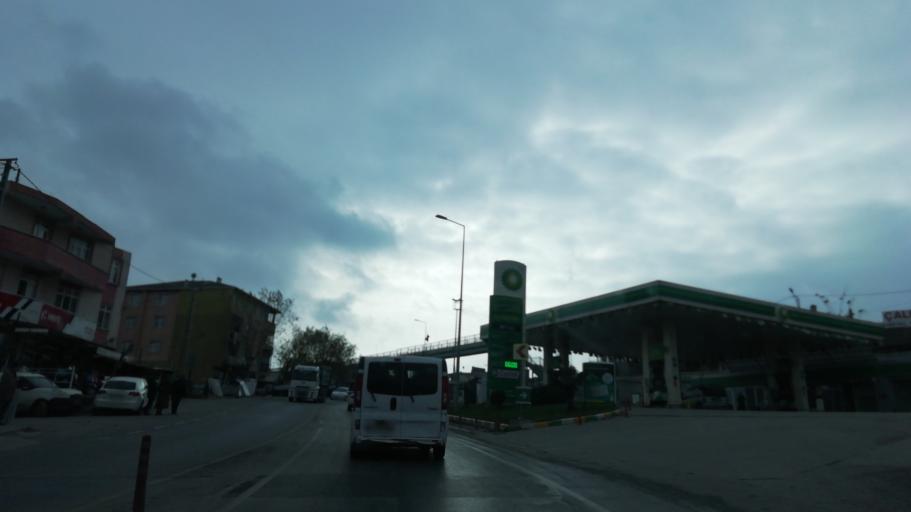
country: TR
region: Istanbul
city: Esenyurt
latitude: 41.0572
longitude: 28.7283
